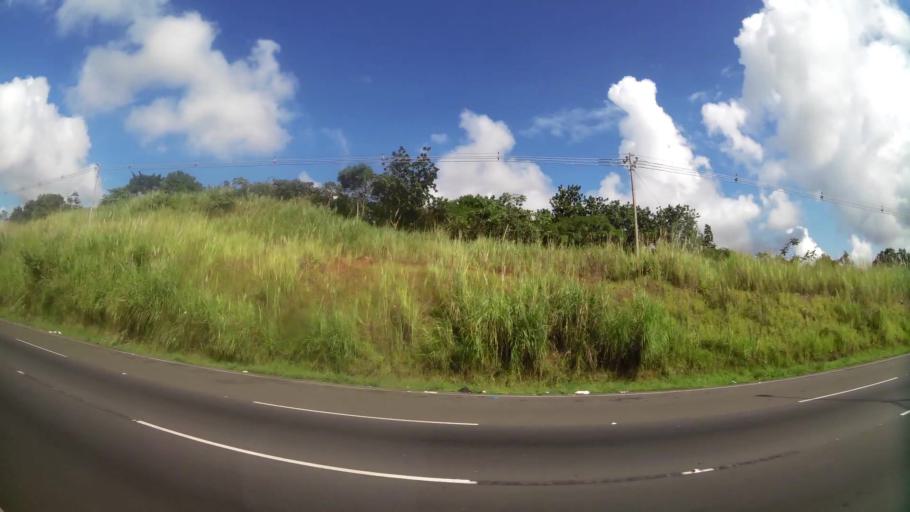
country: PA
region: Panama
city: Nuevo Arraijan
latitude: 8.9099
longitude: -79.7306
